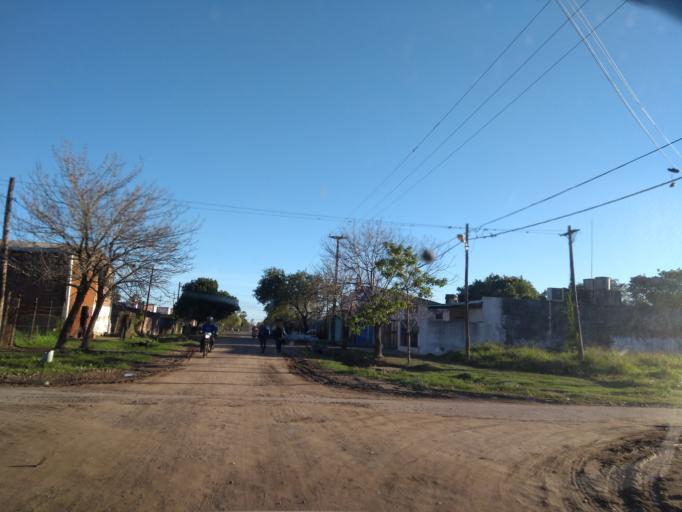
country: AR
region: Chaco
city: Barranqueras
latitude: -27.4883
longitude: -58.9335
